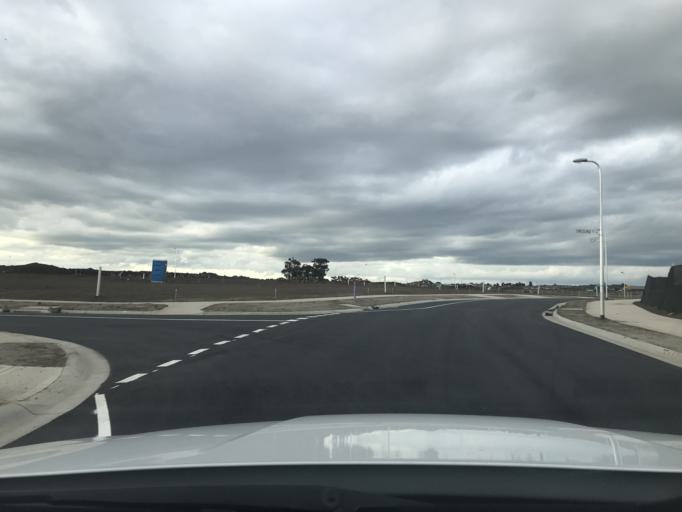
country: AU
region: Victoria
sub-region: Hume
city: Roxburgh Park
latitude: -37.5798
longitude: 144.8995
